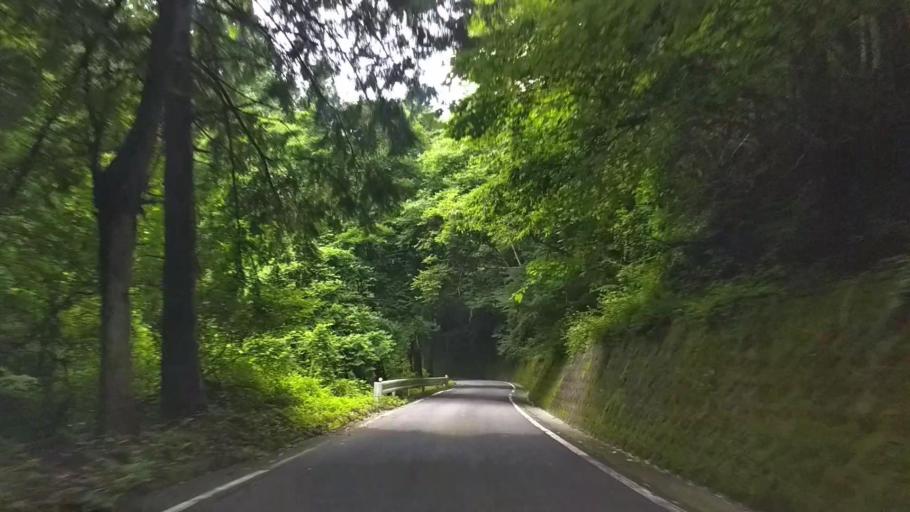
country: JP
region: Shizuoka
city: Gotemba
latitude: 35.3215
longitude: 139.0015
